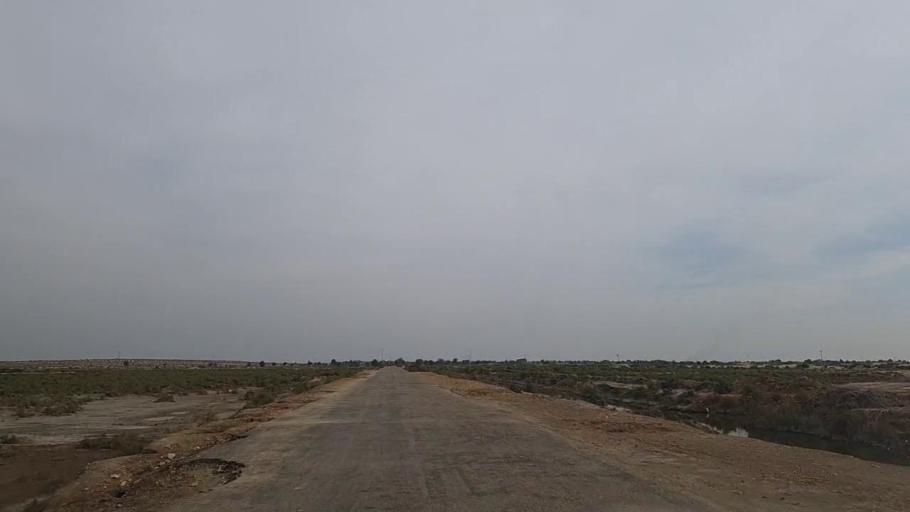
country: PK
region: Sindh
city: Jam Sahib
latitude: 26.4027
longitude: 68.5005
